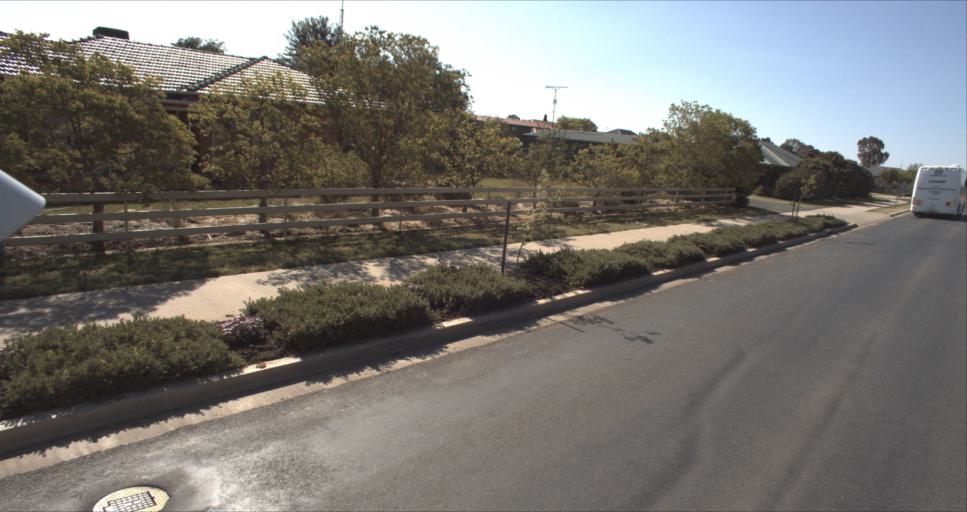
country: AU
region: New South Wales
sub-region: Leeton
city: Leeton
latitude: -34.5546
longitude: 146.4165
